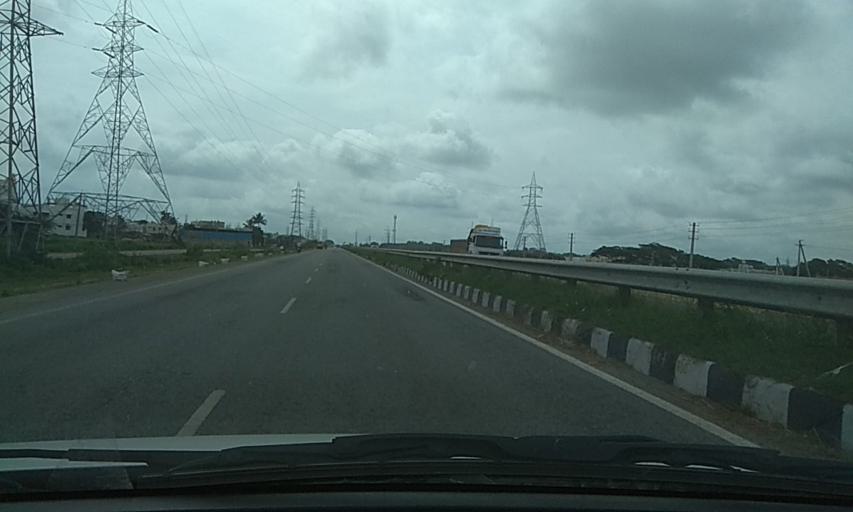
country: IN
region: Karnataka
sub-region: Davanagere
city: Harihar
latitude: 14.4357
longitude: 75.9122
